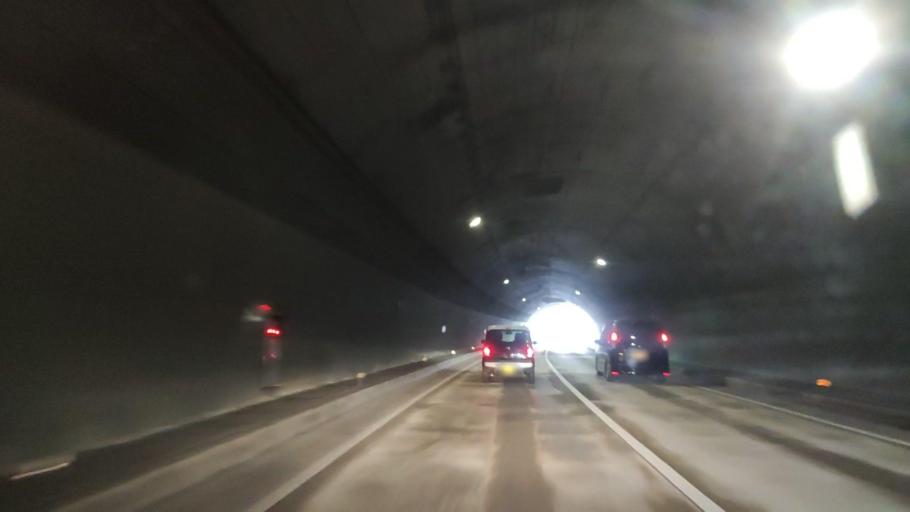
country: JP
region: Hiroshima
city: Onomichi
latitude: 34.4471
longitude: 133.2295
